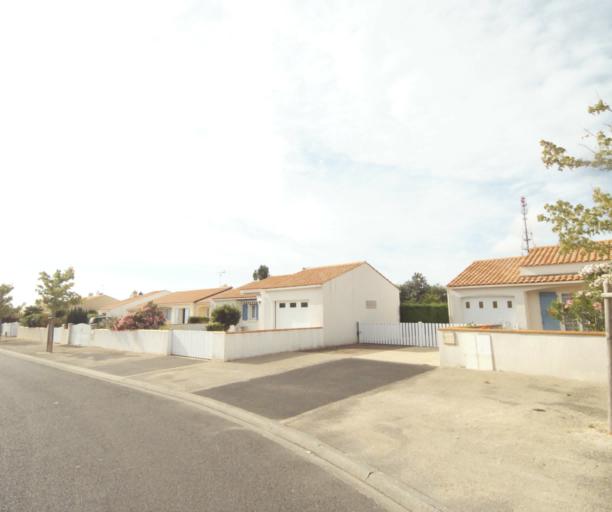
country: FR
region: Pays de la Loire
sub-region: Departement de la Vendee
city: Chateau-d'Olonne
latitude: 46.4889
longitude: -1.7361
